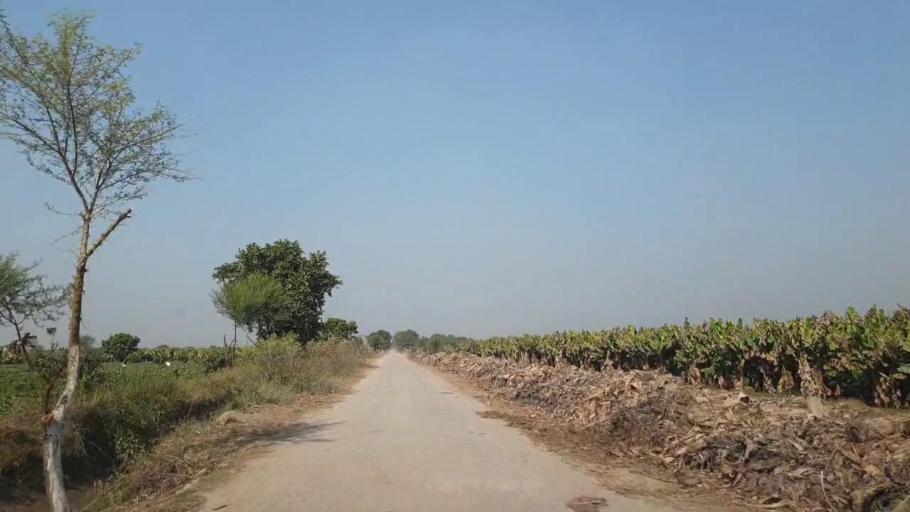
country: PK
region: Sindh
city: Tando Allahyar
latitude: 25.5063
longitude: 68.8221
